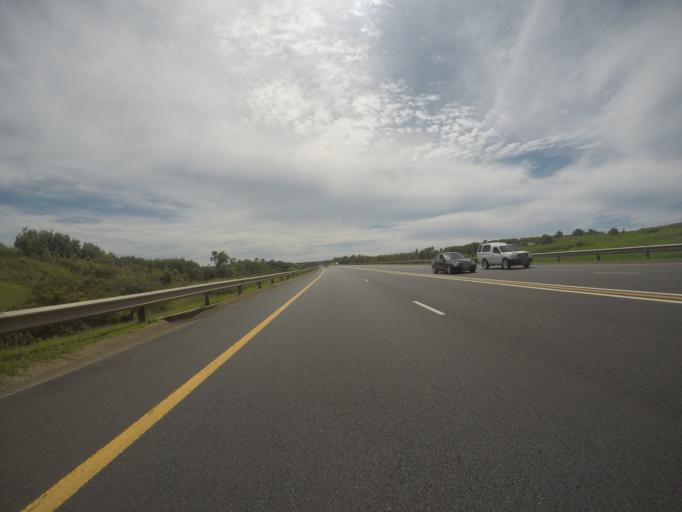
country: ZA
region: KwaZulu-Natal
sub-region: iLembe District Municipality
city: Mandeni
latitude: -29.1651
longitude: 31.5291
